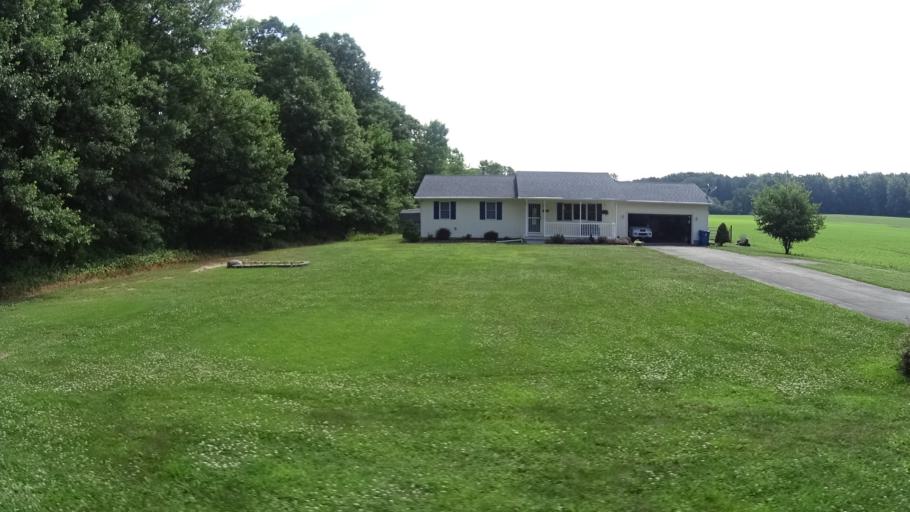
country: US
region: Ohio
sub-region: Lorain County
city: Vermilion
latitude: 41.3754
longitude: -82.4055
